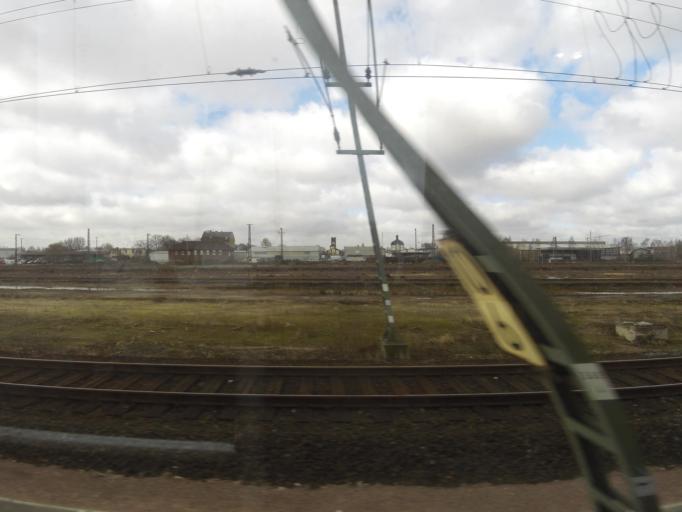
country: DE
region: Hamburg
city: Kleiner Grasbrook
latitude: 53.5074
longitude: 10.0081
